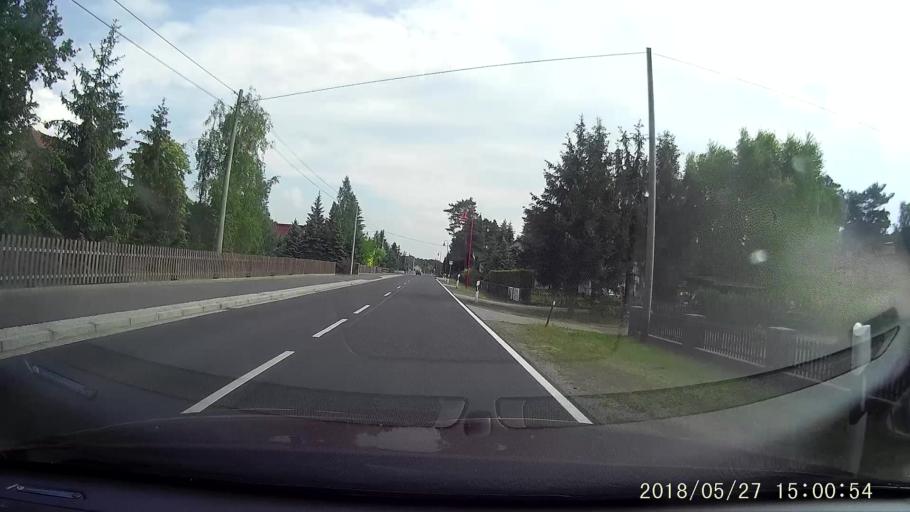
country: DE
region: Saxony
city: Mucka
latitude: 51.3359
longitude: 14.6879
